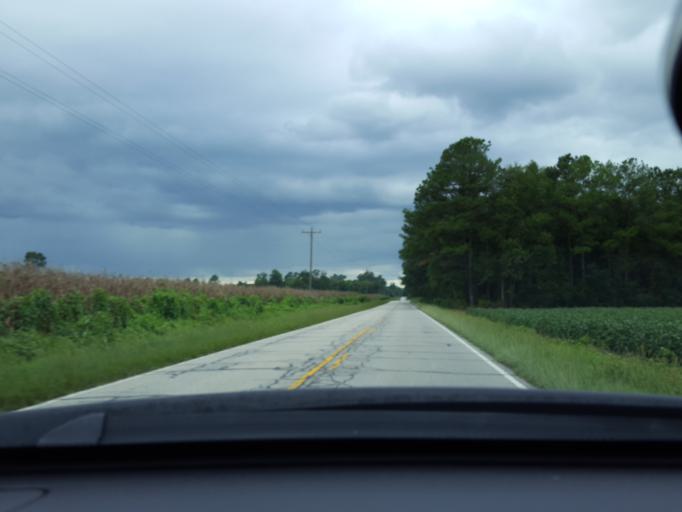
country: US
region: North Carolina
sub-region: Duplin County
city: Rose Hill
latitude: 34.8015
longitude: -78.2215
